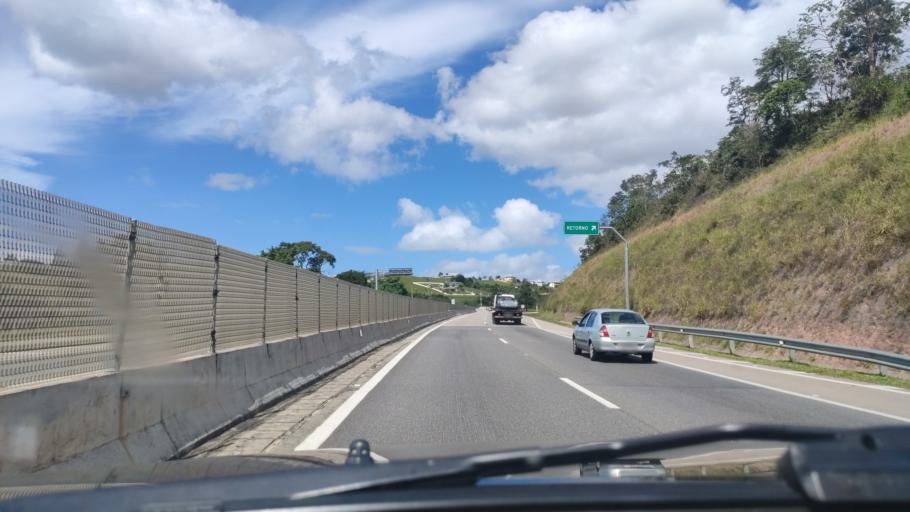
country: BR
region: Sao Paulo
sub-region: Santa Branca
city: Santa Branca
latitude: -23.4345
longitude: -45.6207
